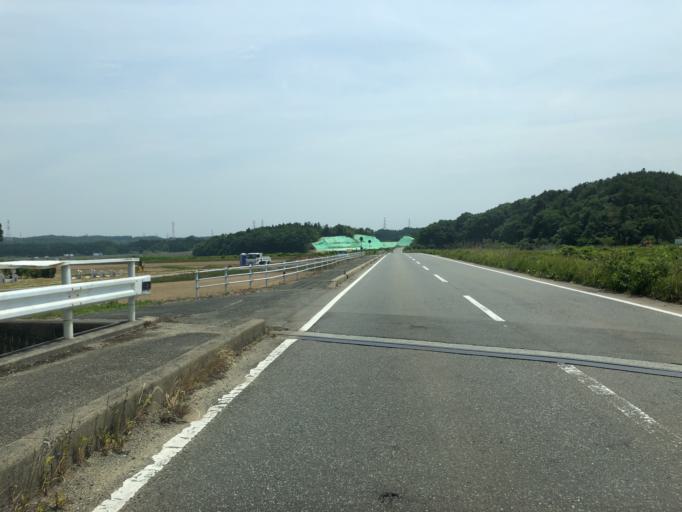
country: JP
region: Fukushima
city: Namie
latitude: 37.5490
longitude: 140.9347
